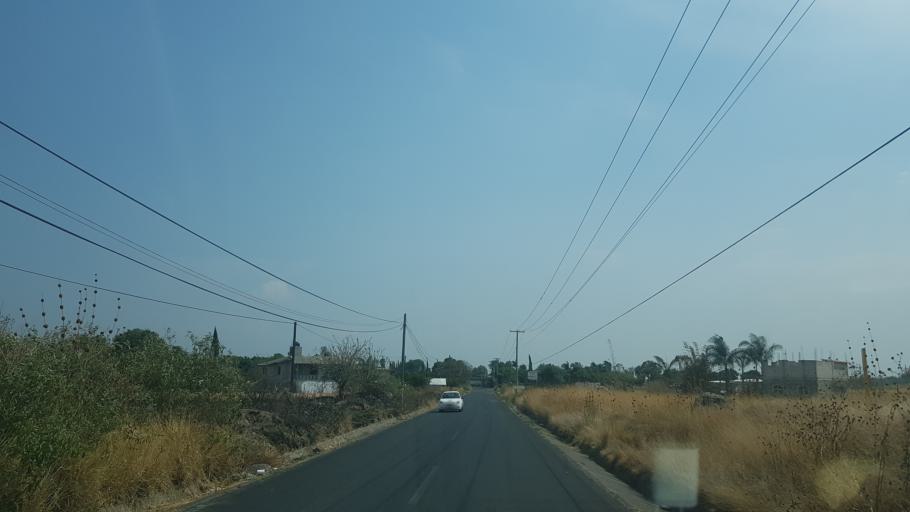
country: MX
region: Puebla
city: Atlixco
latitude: 18.9294
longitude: -98.4543
